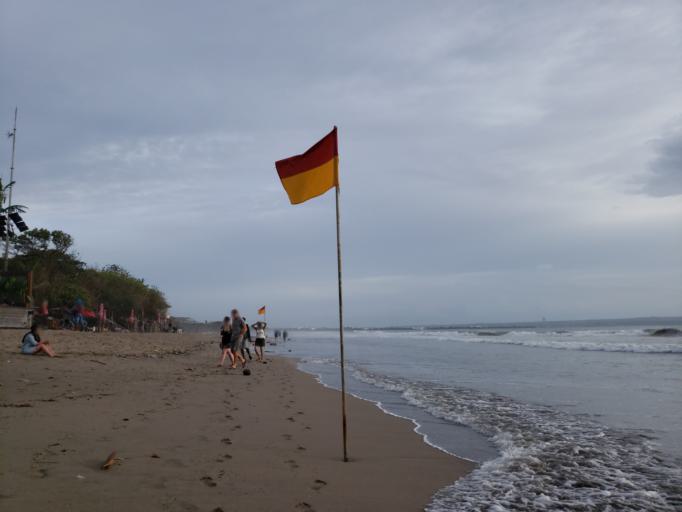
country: ID
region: Bali
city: Kuta
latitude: -8.6871
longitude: 115.1542
